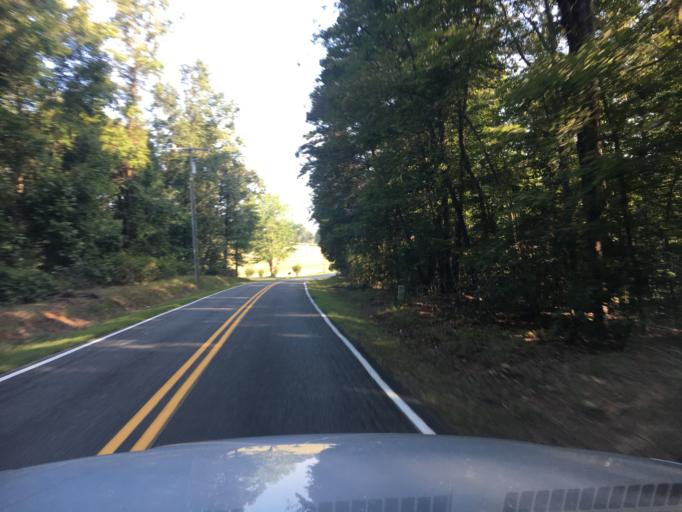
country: US
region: North Carolina
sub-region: Polk County
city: Columbus
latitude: 35.2385
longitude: -82.0533
